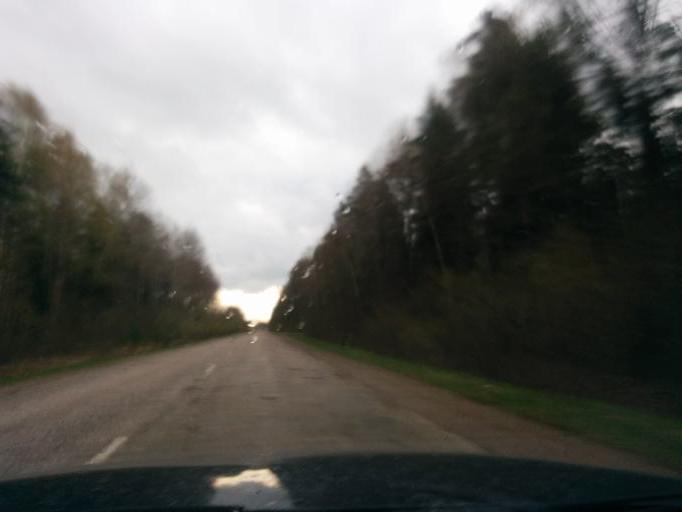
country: LT
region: Siauliu apskritis
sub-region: Joniskis
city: Joniskis
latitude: 56.4162
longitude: 23.6329
